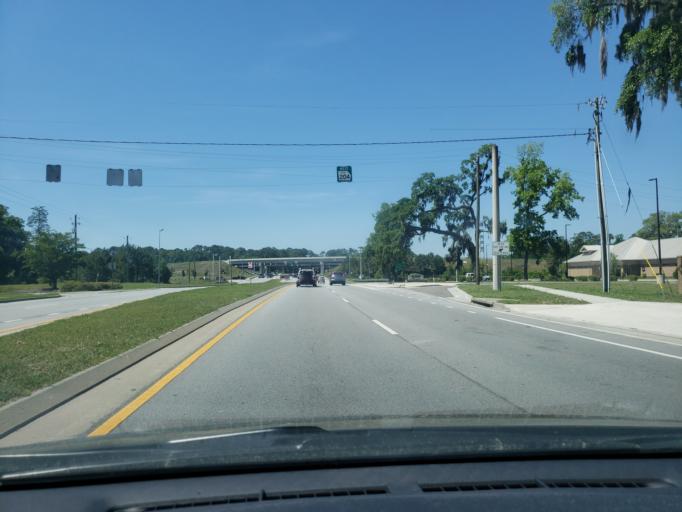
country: US
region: Georgia
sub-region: Chatham County
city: Montgomery
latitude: 31.9707
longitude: -81.1040
